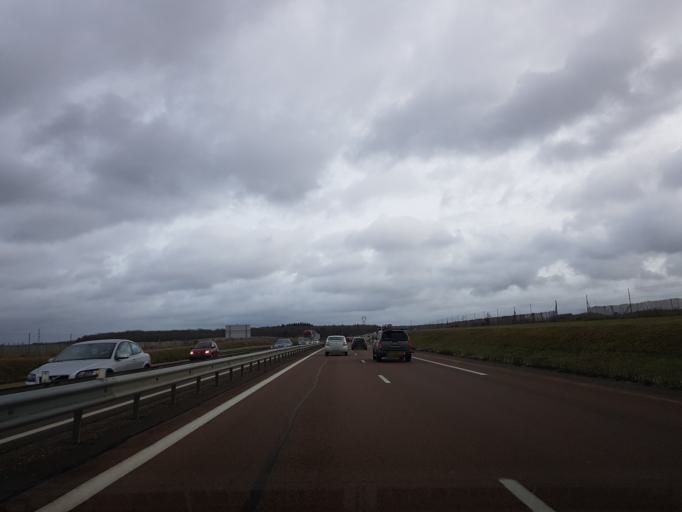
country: FR
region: Champagne-Ardenne
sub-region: Departement de la Haute-Marne
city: Chamarandes-Choignes
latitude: 48.0411
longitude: 5.0431
